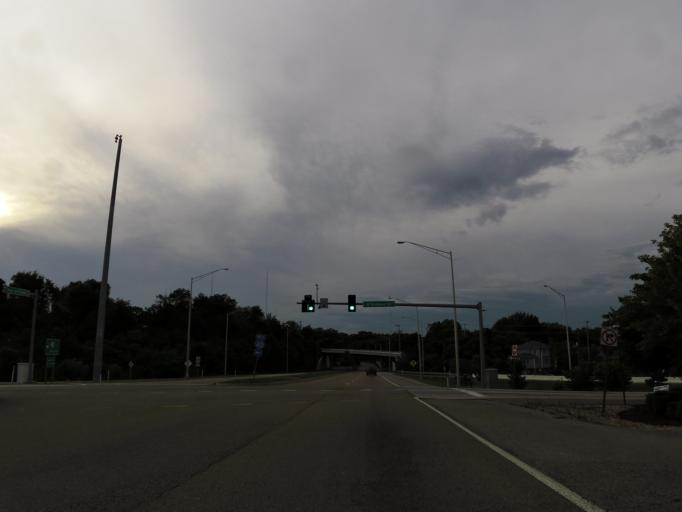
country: US
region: Tennessee
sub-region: Knox County
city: Knoxville
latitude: 35.9838
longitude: -83.9178
